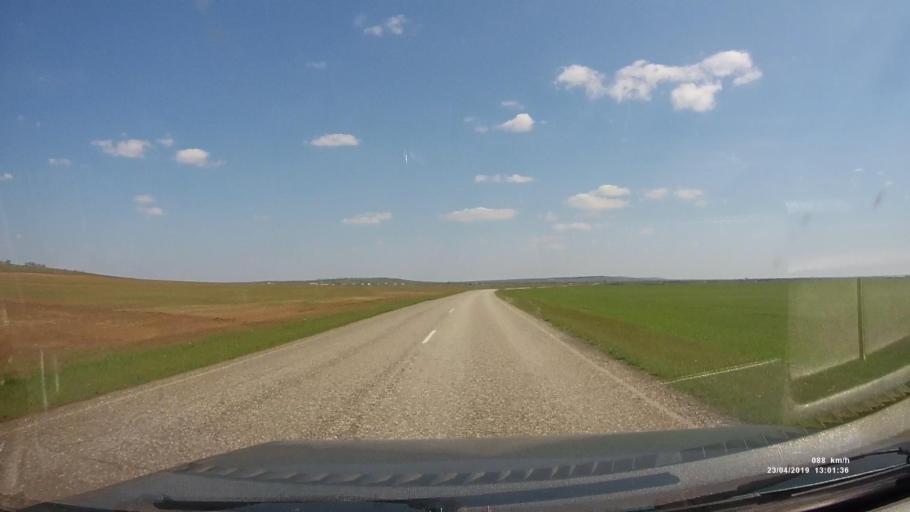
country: RU
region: Kalmykiya
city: Yashalta
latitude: 46.6038
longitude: 42.6553
